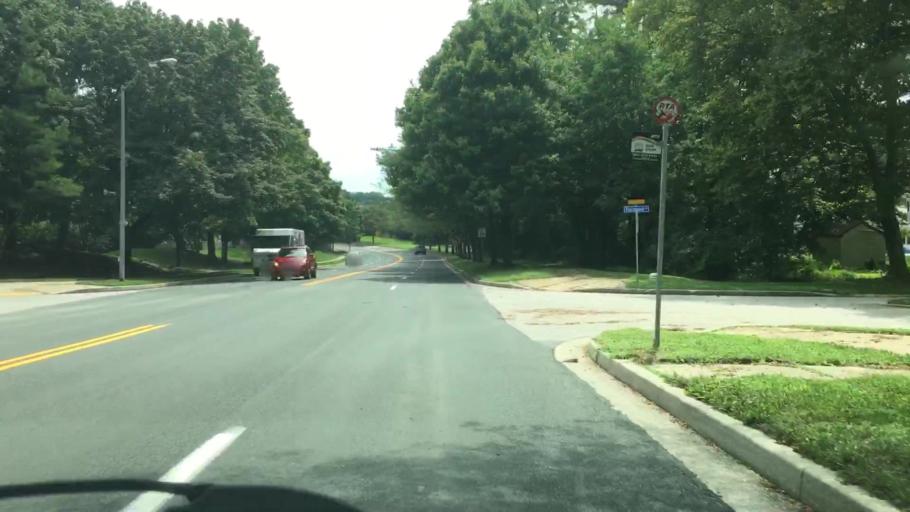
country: US
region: Maryland
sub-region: Howard County
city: Columbia
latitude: 39.1974
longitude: -76.8348
